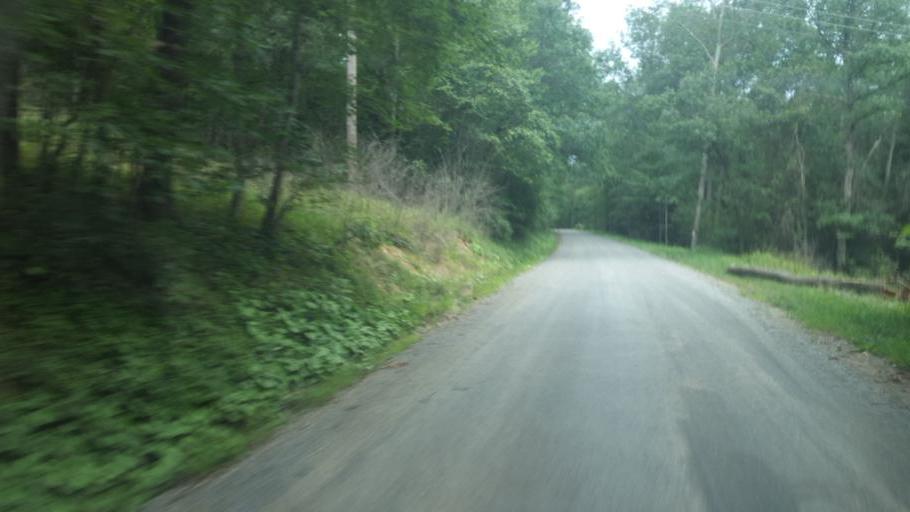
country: US
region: Pennsylvania
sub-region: Clarion County
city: Marianne
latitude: 41.2225
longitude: -79.4140
